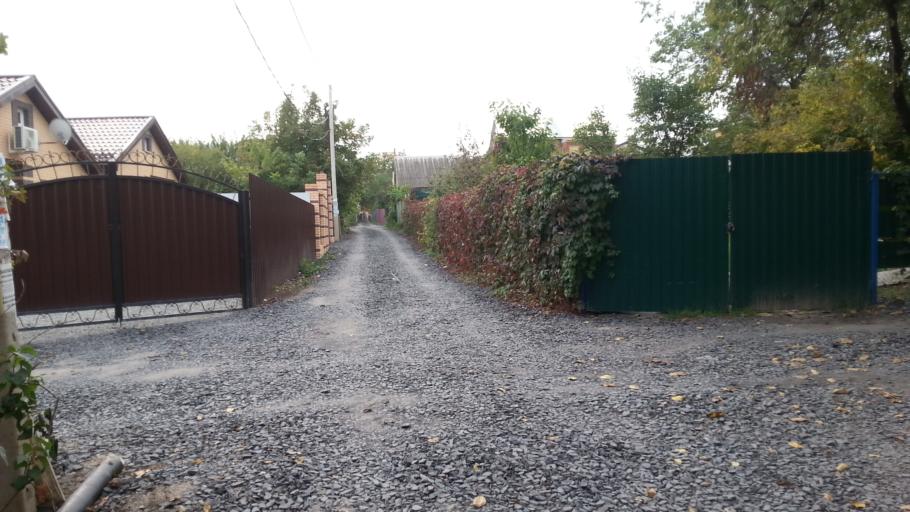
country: RU
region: Rostov
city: Severnyy
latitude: 47.2908
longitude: 39.6674
